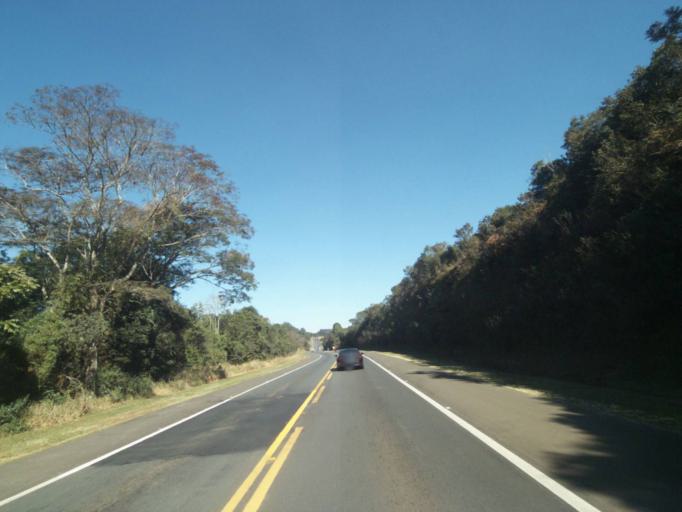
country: BR
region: Parana
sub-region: Tibagi
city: Tibagi
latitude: -24.7348
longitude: -50.5371
